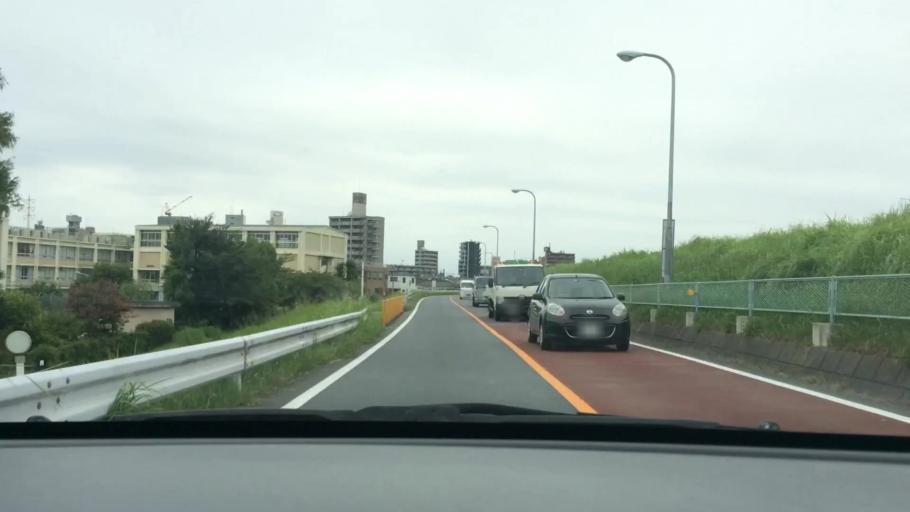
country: JP
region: Chiba
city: Matsudo
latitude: 35.7655
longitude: 139.8787
